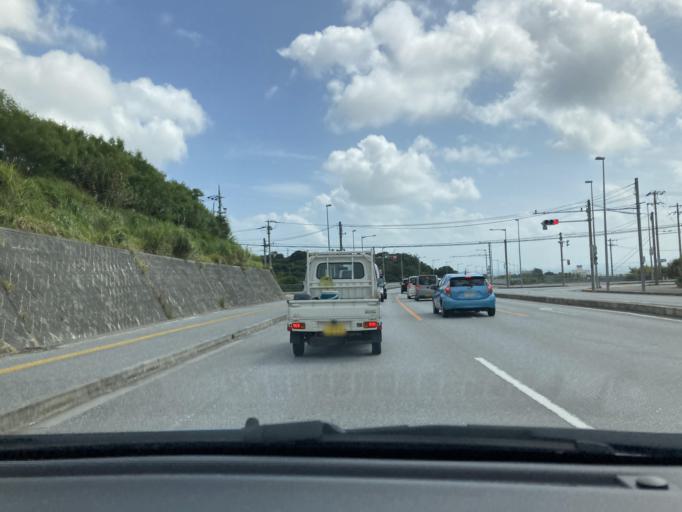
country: JP
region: Okinawa
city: Okinawa
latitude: 26.3164
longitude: 127.7983
